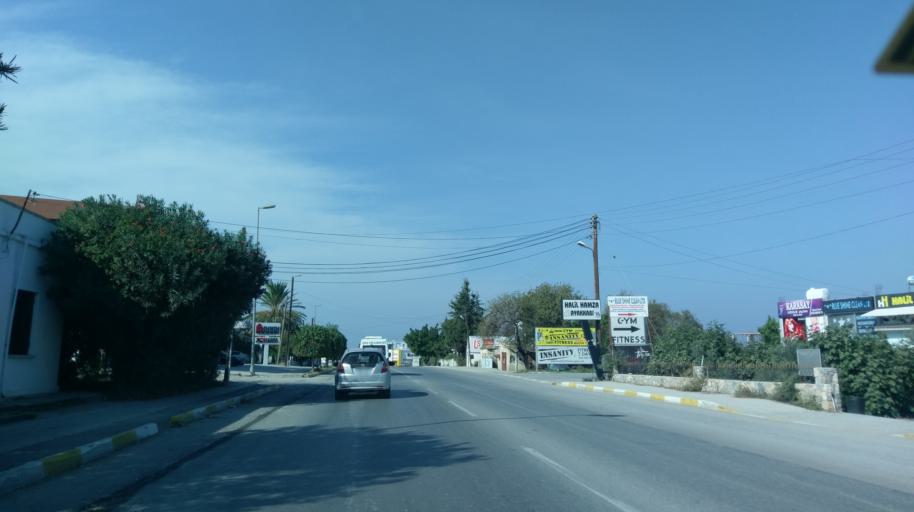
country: CY
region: Keryneia
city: Kyrenia
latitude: 35.3413
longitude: 33.2844
